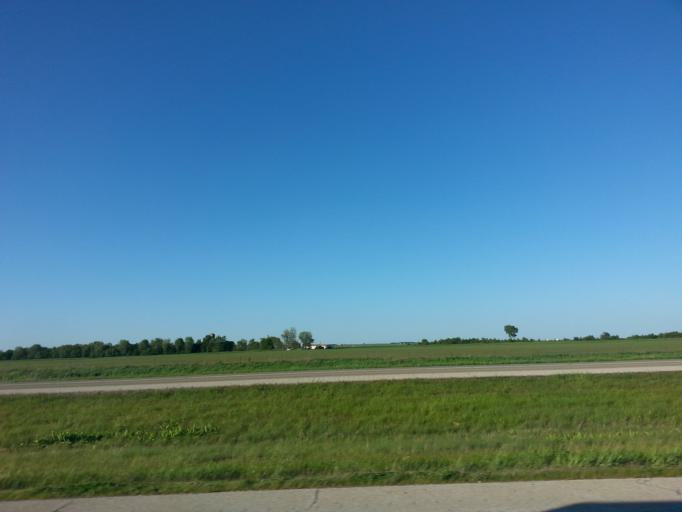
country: US
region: Illinois
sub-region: McLean County
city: Le Roy
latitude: 40.3002
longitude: -88.7121
